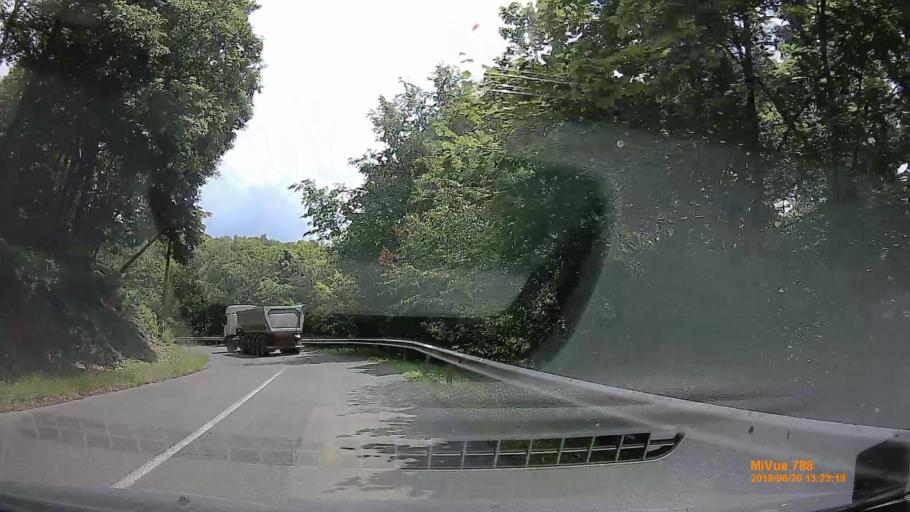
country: HU
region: Baranya
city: Hosszuheteny
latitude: 46.1751
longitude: 18.3241
